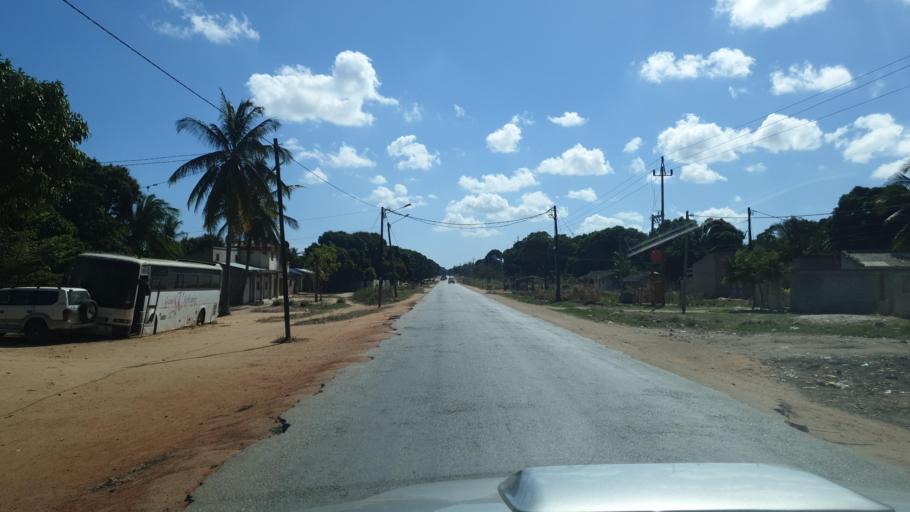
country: MZ
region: Nampula
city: Nacala
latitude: -14.5173
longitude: 40.6961
